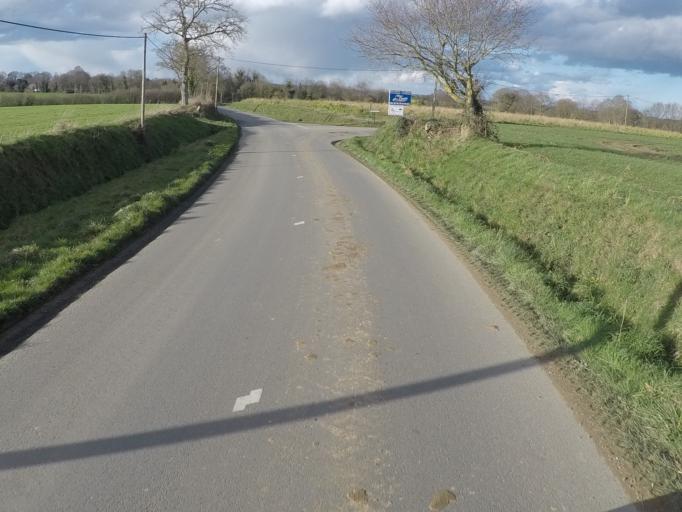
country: FR
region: Brittany
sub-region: Departement des Cotes-d'Armor
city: Plelo
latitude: 48.5653
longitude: -2.9788
